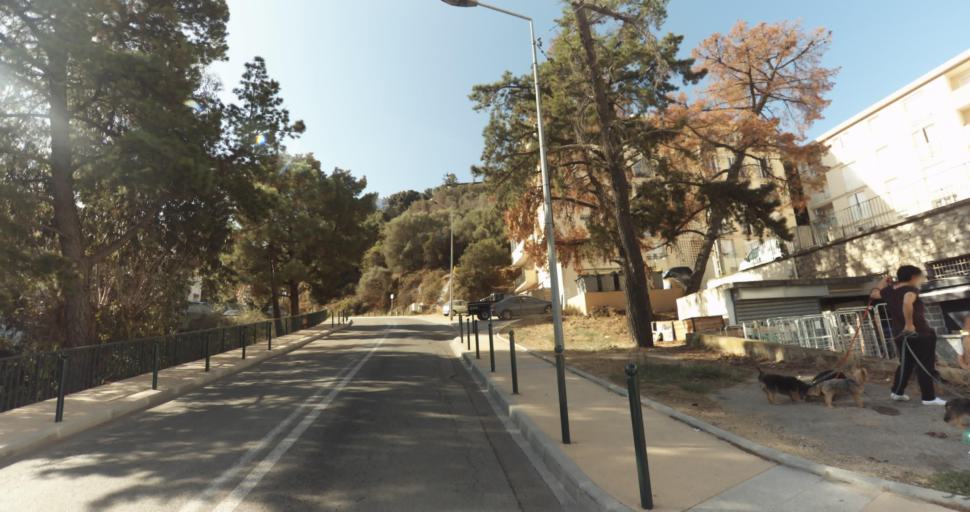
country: FR
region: Corsica
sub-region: Departement de la Corse-du-Sud
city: Ajaccio
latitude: 41.9261
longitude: 8.7287
